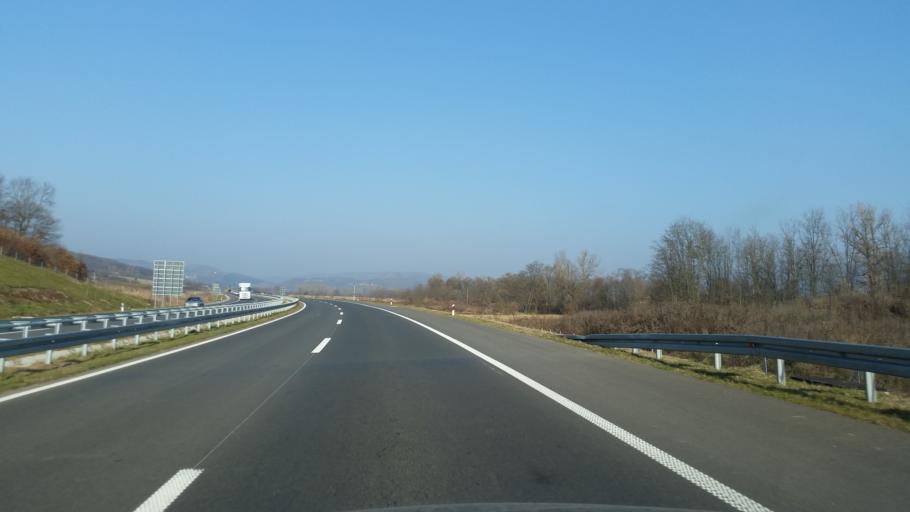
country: RS
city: Prislonica
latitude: 43.9281
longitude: 20.4018
